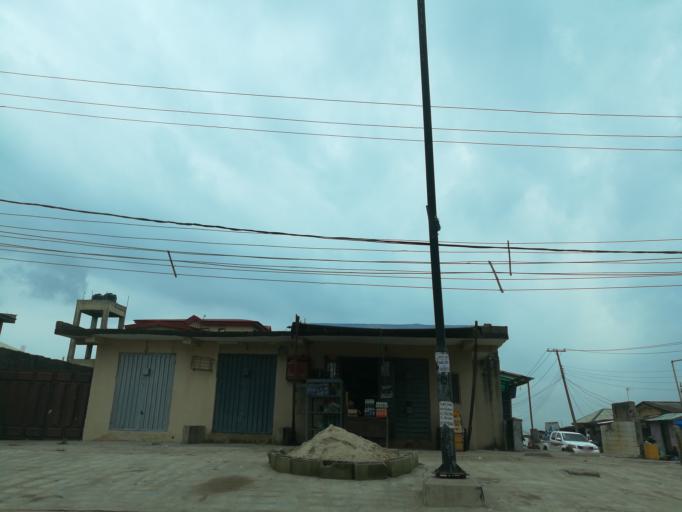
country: NG
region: Lagos
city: Ojota
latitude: 6.6200
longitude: 3.3962
